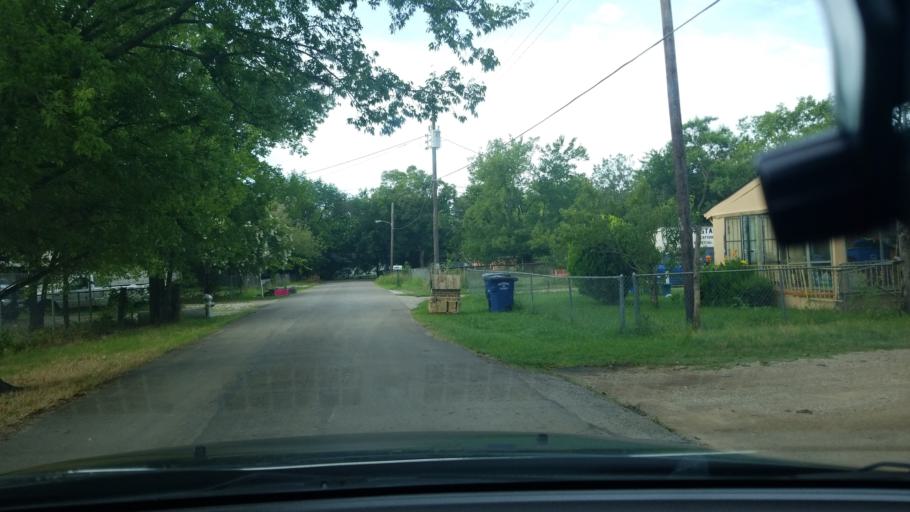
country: US
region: Texas
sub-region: Dallas County
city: Balch Springs
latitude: 32.7614
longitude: -96.6466
